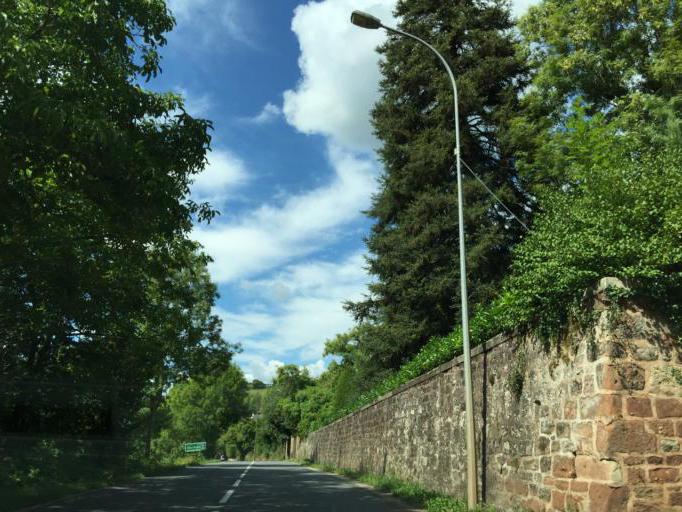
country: FR
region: Midi-Pyrenees
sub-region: Departement de l'Aveyron
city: Marcillac-Vallon
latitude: 44.4651
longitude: 2.4690
